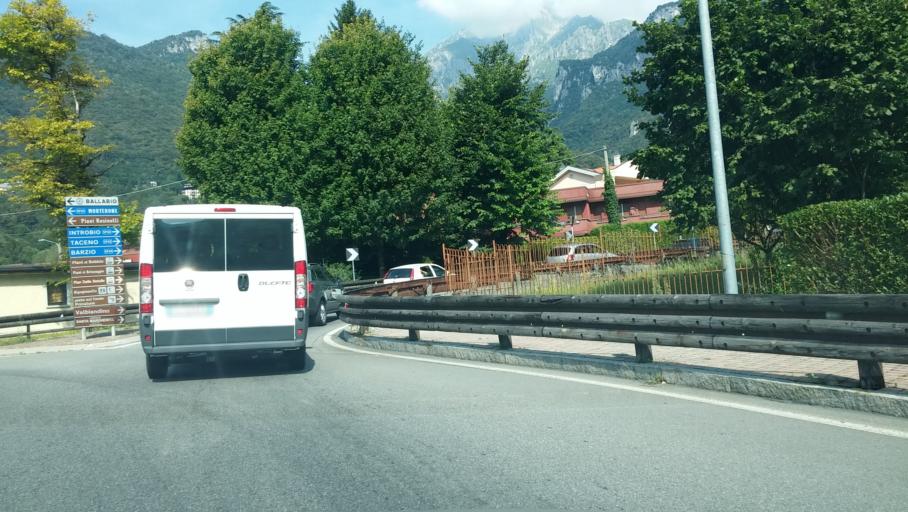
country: IT
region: Lombardy
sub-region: Provincia di Lecco
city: Ballabio
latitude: 45.8964
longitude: 9.4256
